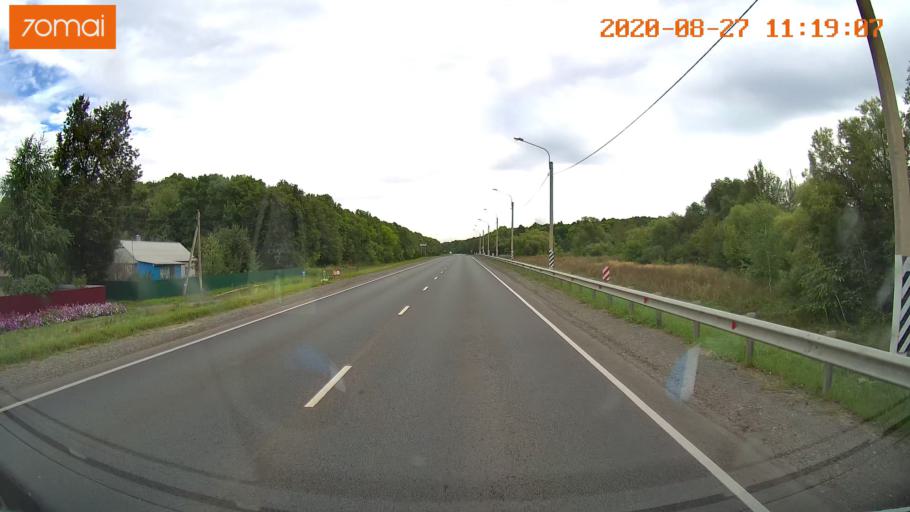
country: RU
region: Rjazan
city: Oktyabr'skiy
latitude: 54.1822
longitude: 38.9091
